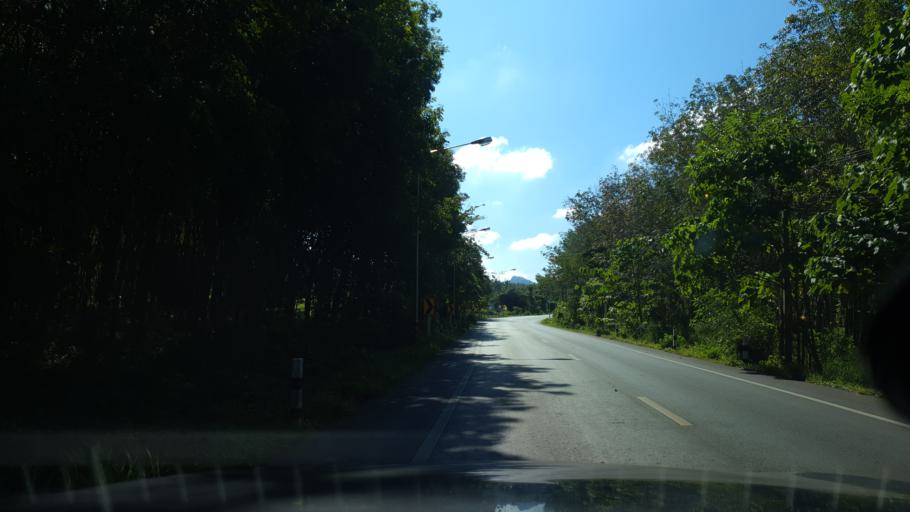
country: TH
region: Phangnga
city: Ban Ao Nang
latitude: 8.0746
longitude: 98.8060
